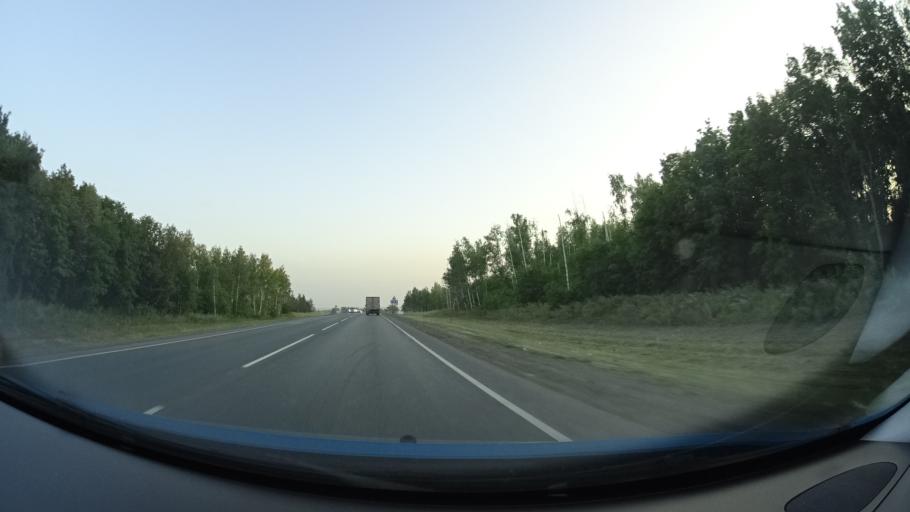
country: RU
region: Samara
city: Sernovodsk
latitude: 53.9171
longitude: 51.3052
